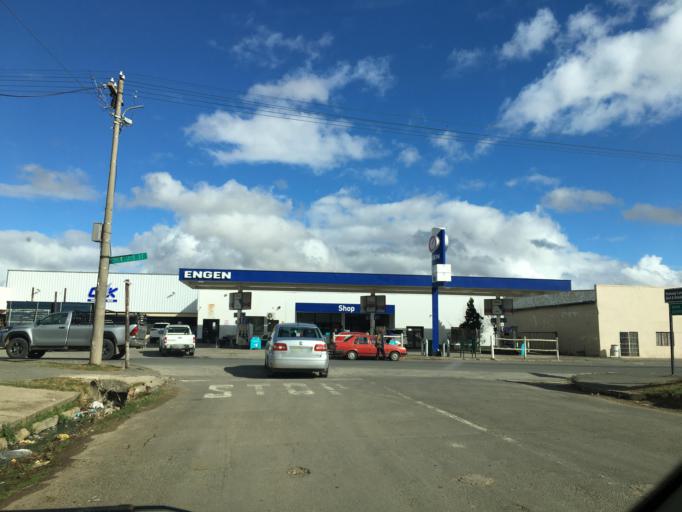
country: ZA
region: Eastern Cape
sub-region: Chris Hani District Municipality
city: Elliot
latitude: -31.3326
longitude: 27.8535
